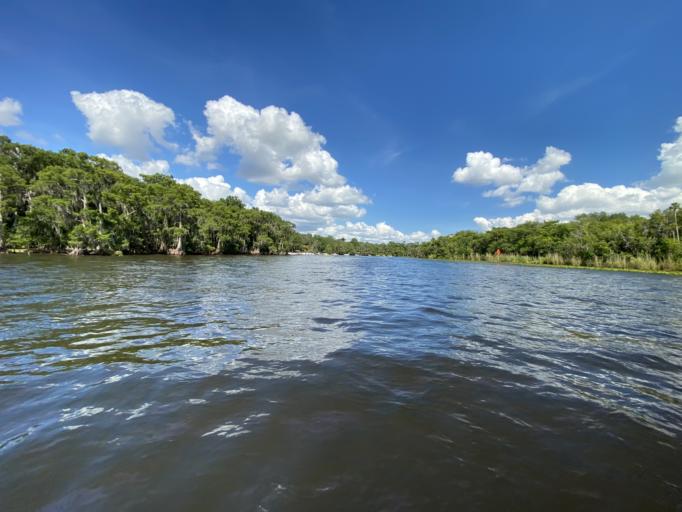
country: US
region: Florida
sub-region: Volusia County
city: DeBary
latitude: 28.8635
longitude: -81.3557
